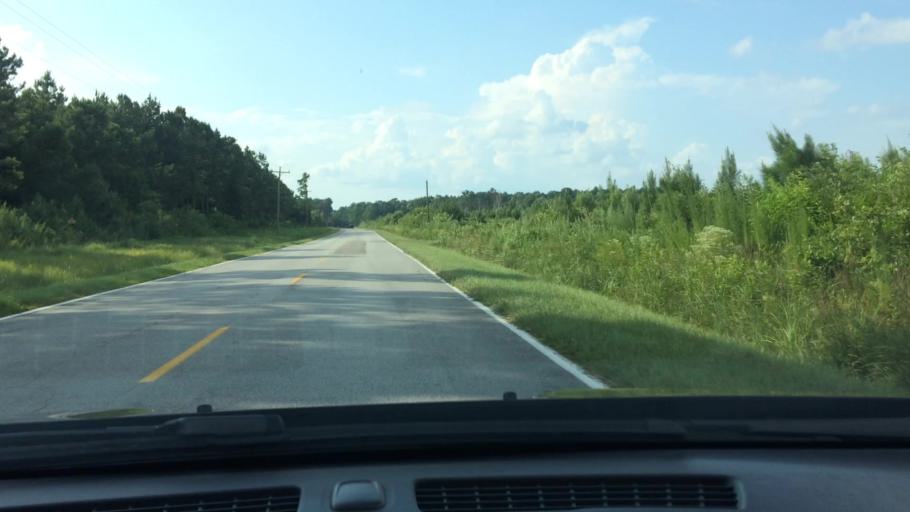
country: US
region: North Carolina
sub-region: Beaufort County
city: River Road
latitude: 35.4432
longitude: -77.0127
